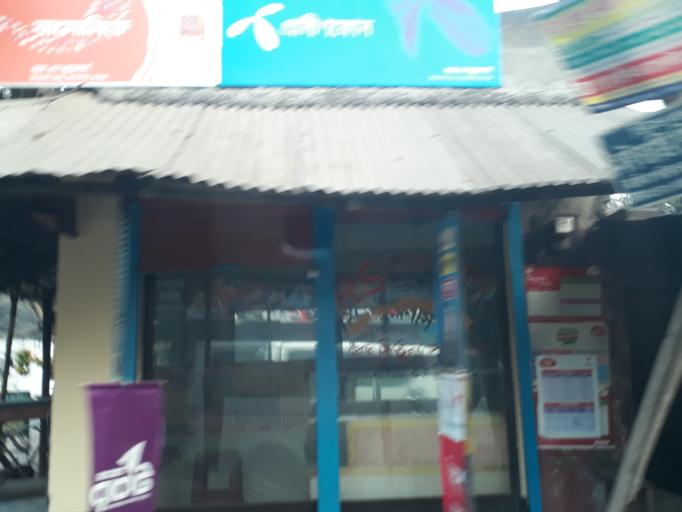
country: BD
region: Khulna
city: Bhatpara Abhaynagar
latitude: 23.0229
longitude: 89.4055
